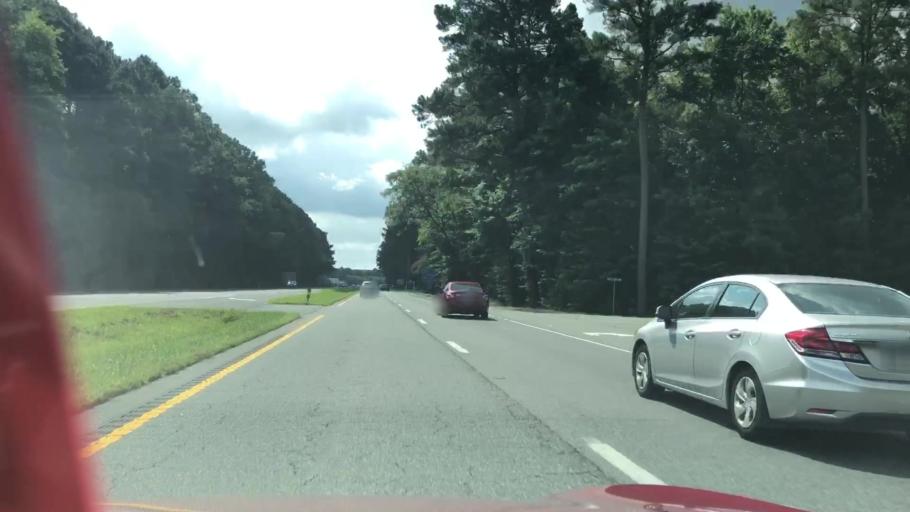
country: US
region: Virginia
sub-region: Accomack County
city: Wattsville
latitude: 37.9926
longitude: -75.5358
